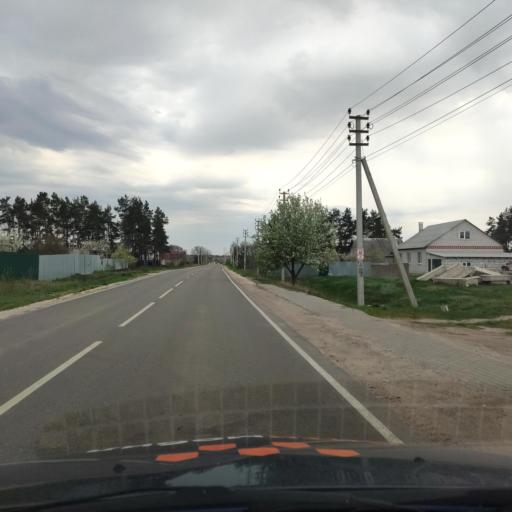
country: RU
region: Voronezj
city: Podgornoye
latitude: 51.8773
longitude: 39.1730
